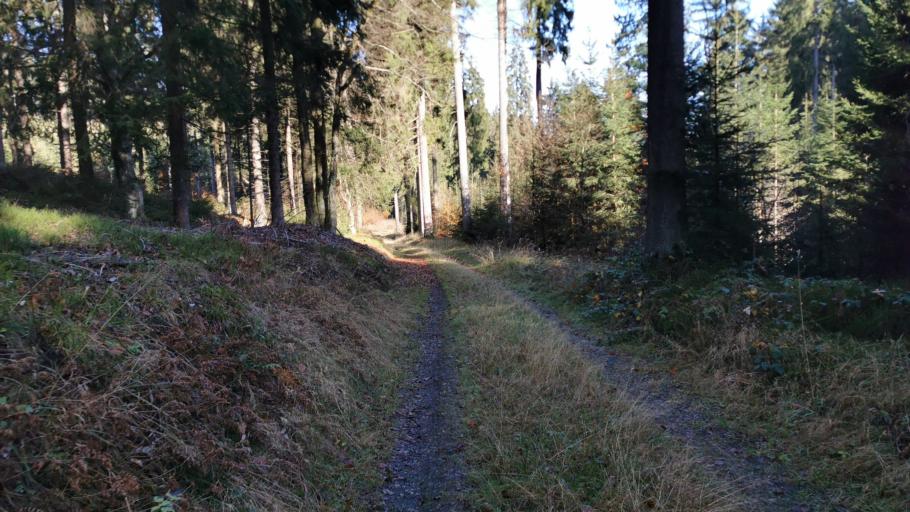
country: DE
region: Bavaria
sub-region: Upper Franconia
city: Reichenbach
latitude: 50.4472
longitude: 11.4289
